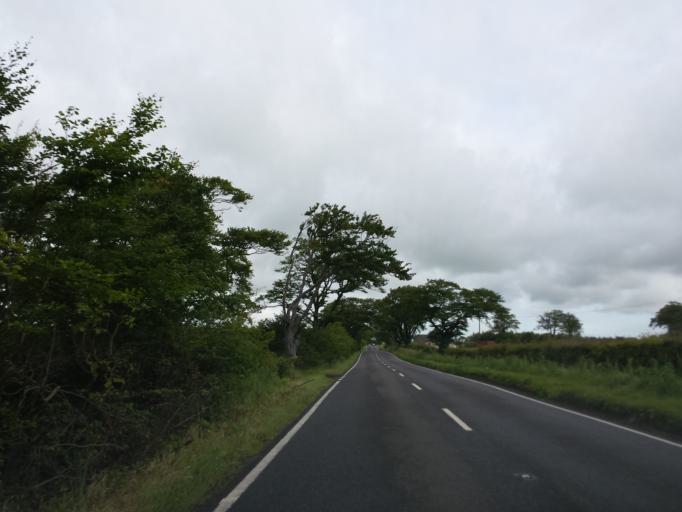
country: GB
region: Scotland
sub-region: Fife
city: Strathkinness
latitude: 56.2815
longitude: -2.8396
